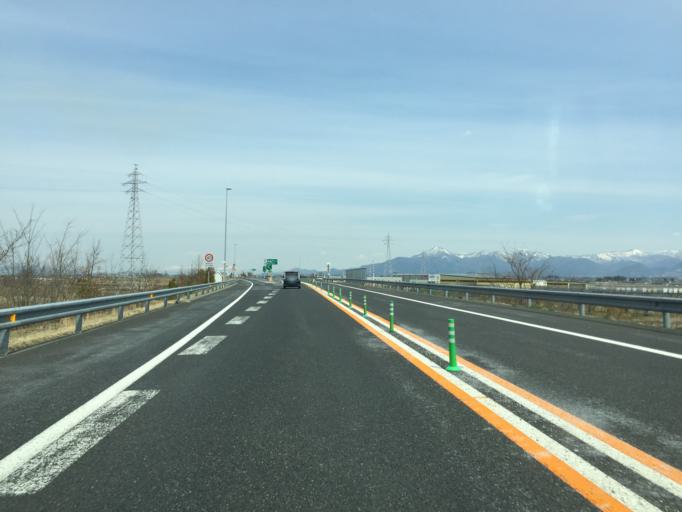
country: JP
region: Yamagata
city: Tendo
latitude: 38.3599
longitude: 140.3446
